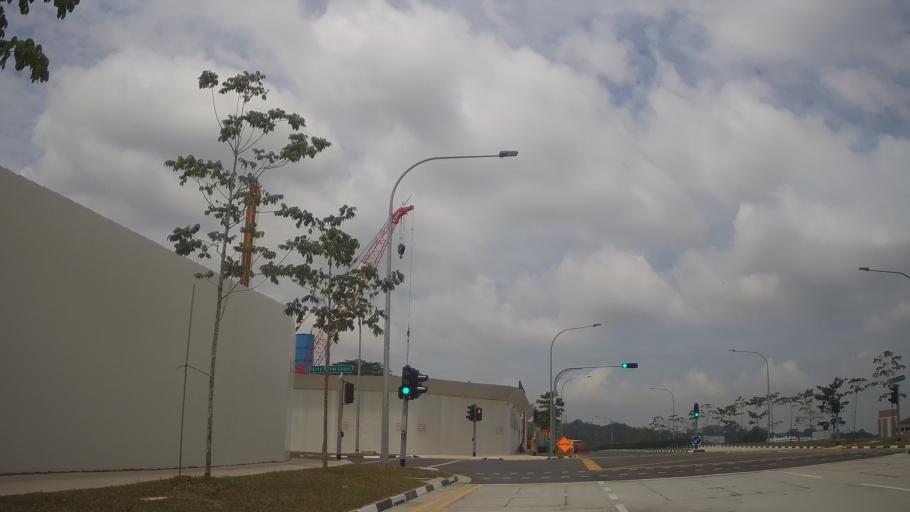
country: MY
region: Johor
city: Johor Bahru
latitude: 1.3669
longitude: 103.7745
